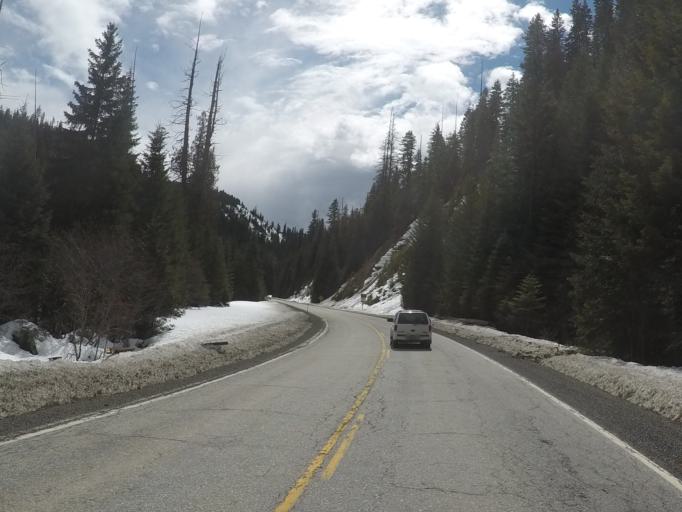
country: US
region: Montana
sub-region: Ravalli County
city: Stevensville
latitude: 46.5443
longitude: -114.6756
